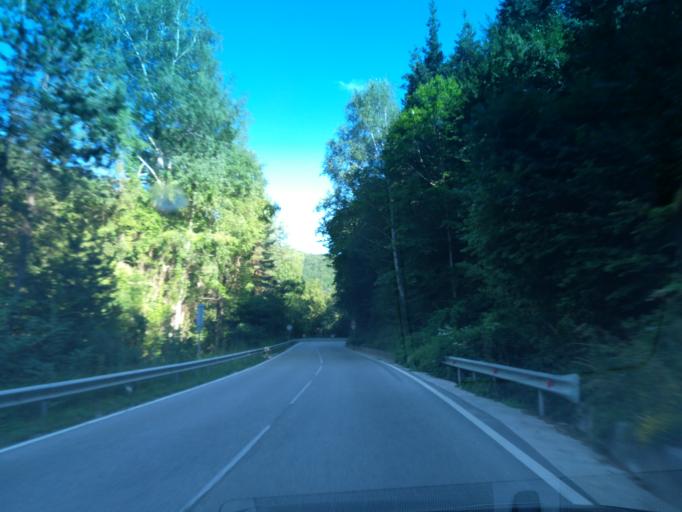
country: BG
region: Smolyan
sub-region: Obshtina Chepelare
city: Chepelare
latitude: 41.8125
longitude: 24.7041
